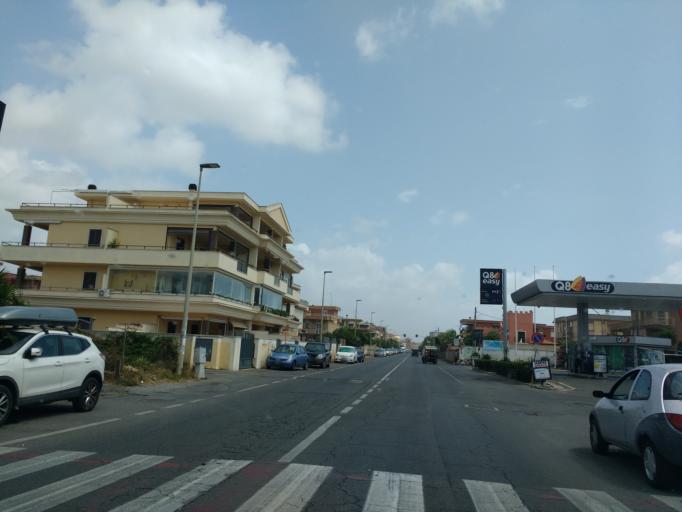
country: IT
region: Latium
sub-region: Citta metropolitana di Roma Capitale
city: Torvaianica
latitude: 41.6472
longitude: 12.4301
